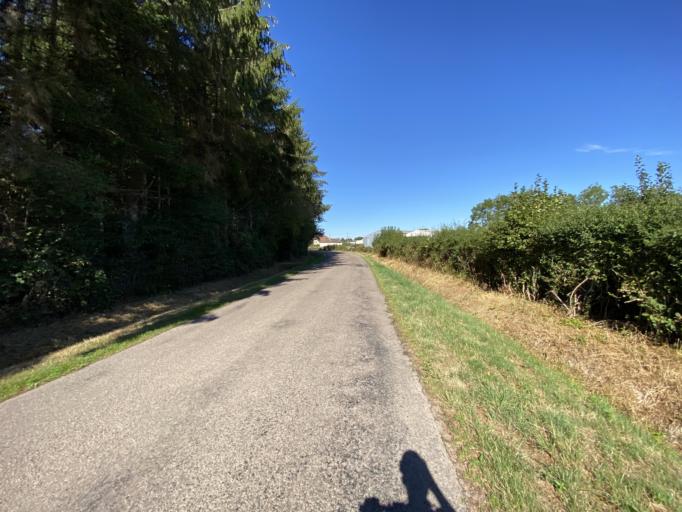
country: FR
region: Bourgogne
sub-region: Departement de la Cote-d'Or
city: Saulieu
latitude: 47.2760
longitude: 4.1976
